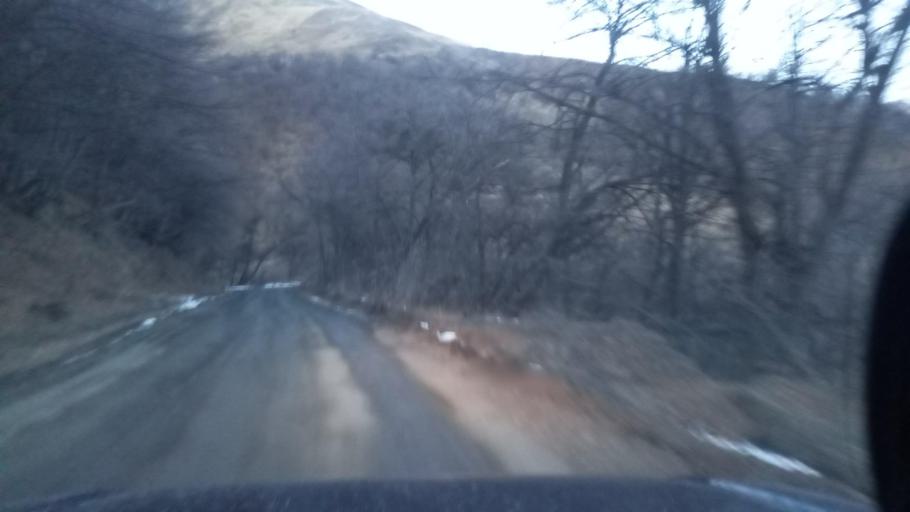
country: RU
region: Ingushetiya
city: Dzhayrakh
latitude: 42.8294
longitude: 44.5858
